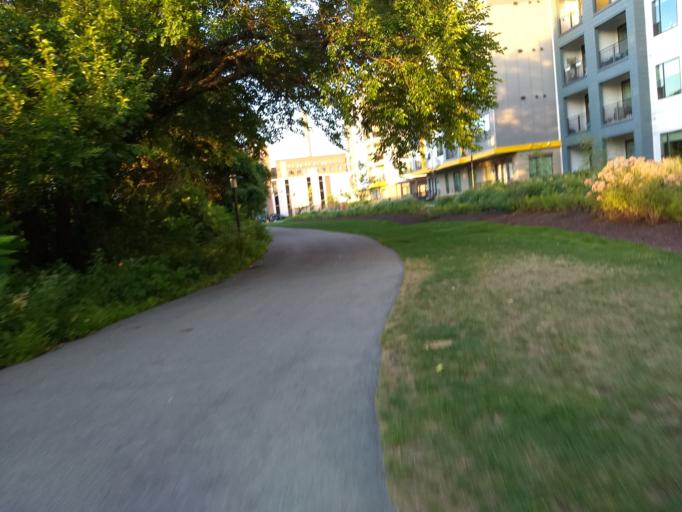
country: US
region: Pennsylvania
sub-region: Allegheny County
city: Pittsburgh
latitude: 40.4529
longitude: -79.9865
